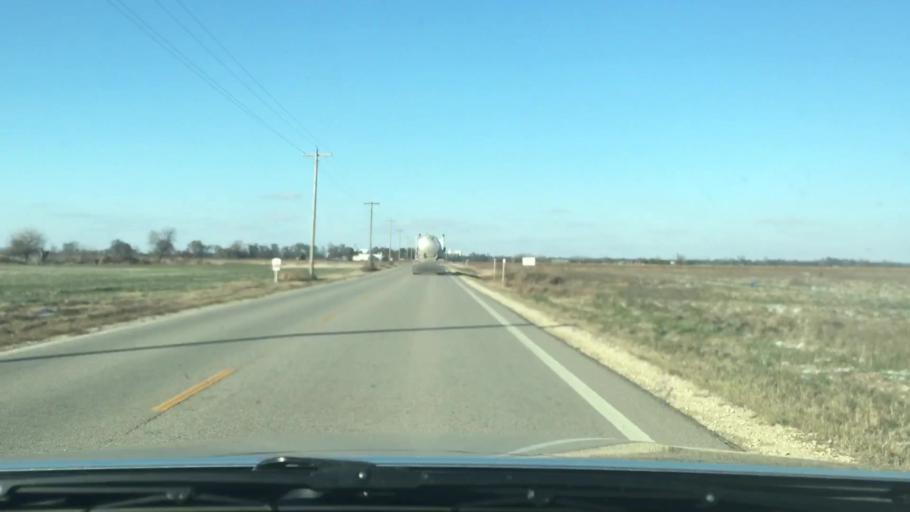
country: US
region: Kansas
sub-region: Rice County
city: Sterling
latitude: 38.1795
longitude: -98.2068
